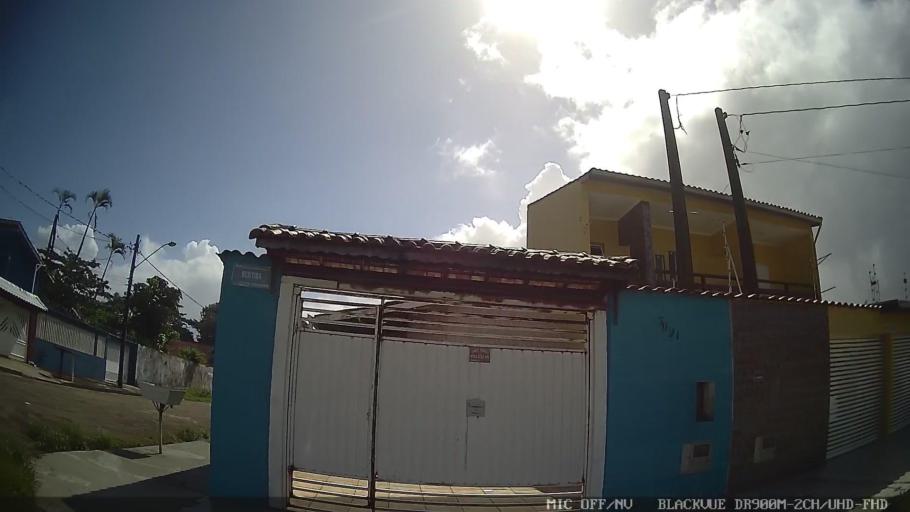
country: BR
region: Sao Paulo
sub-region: Itanhaem
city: Itanhaem
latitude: -24.1699
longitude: -46.7596
